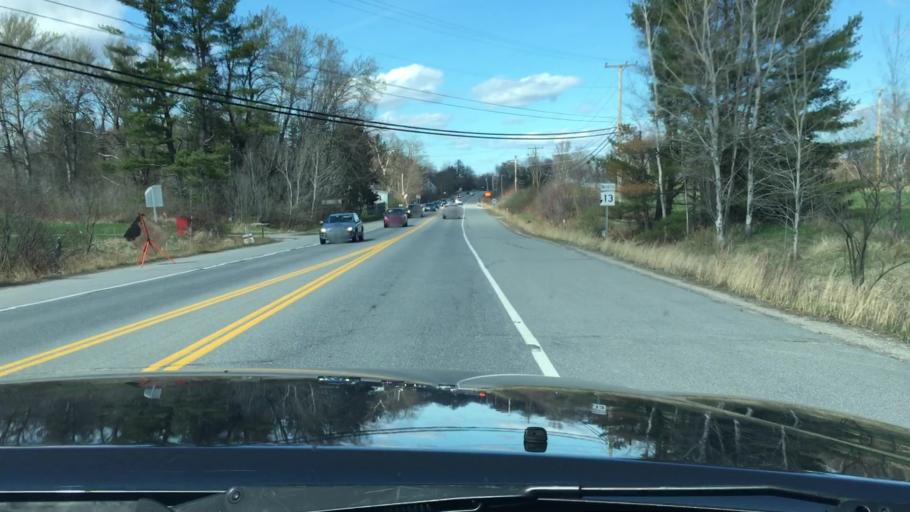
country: US
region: New Hampshire
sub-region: Merrimack County
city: Concord
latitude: 43.1828
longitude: -71.5630
